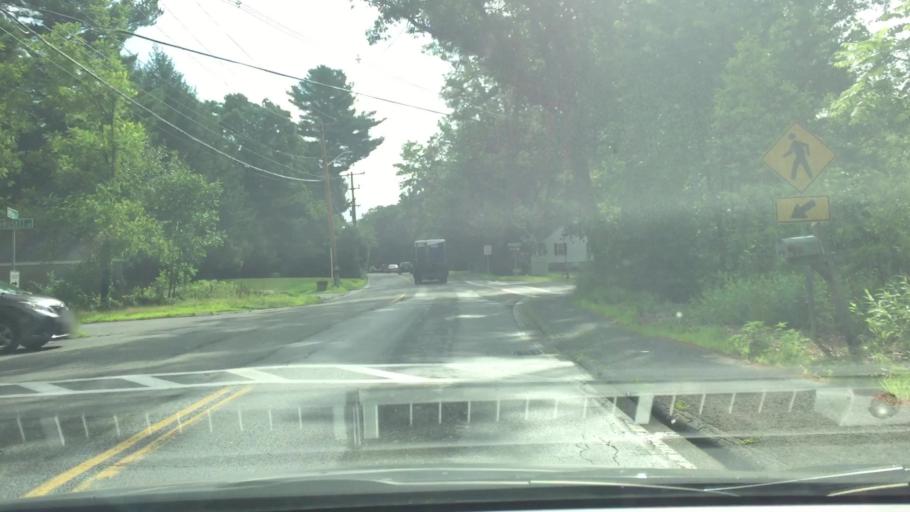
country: US
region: Massachusetts
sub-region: Middlesex County
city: Acton
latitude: 42.4815
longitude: -71.4430
